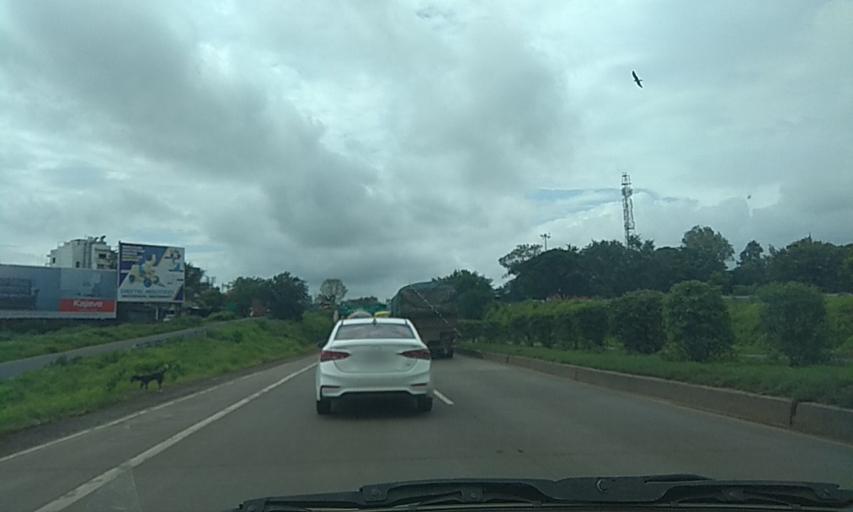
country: IN
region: Maharashtra
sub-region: Kolhapur
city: Kagal
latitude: 16.6372
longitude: 74.2811
